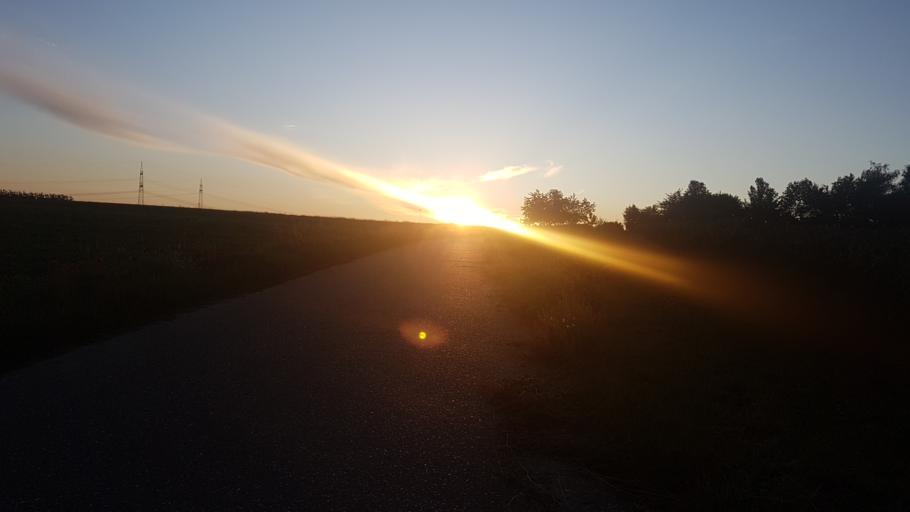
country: DE
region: Baden-Wuerttemberg
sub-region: Regierungsbezirk Stuttgart
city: Guglingen
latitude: 49.0938
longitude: 8.9996
